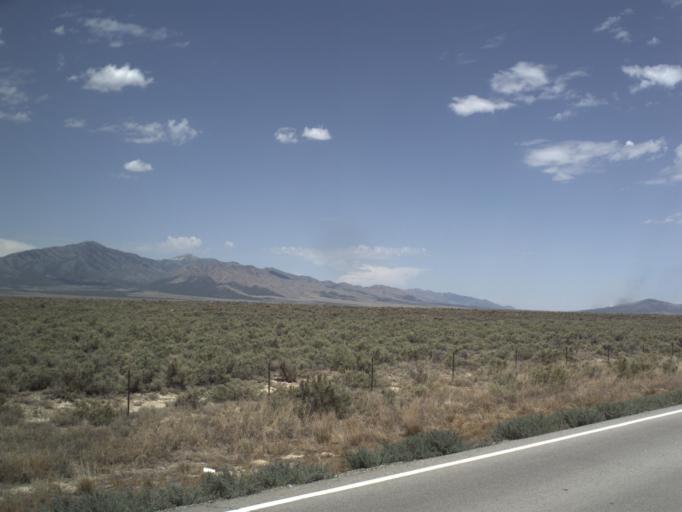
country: US
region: Utah
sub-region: Tooele County
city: Tooele
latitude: 40.2453
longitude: -112.4004
